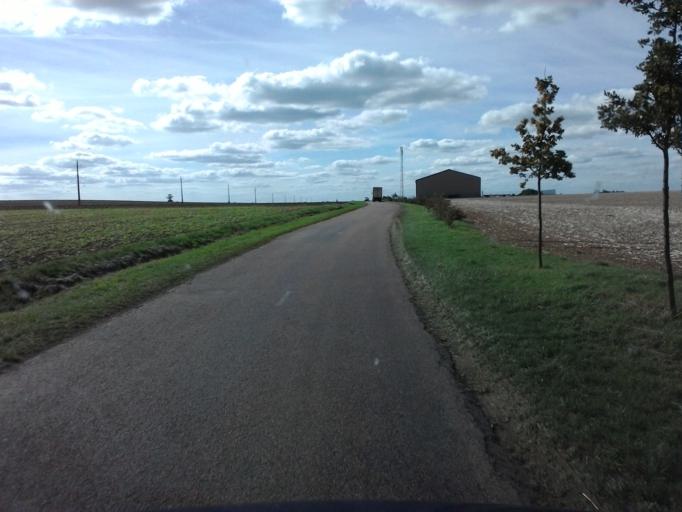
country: FR
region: Bourgogne
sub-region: Departement de la Cote-d'Or
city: Montbard
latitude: 47.7327
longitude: 4.4415
